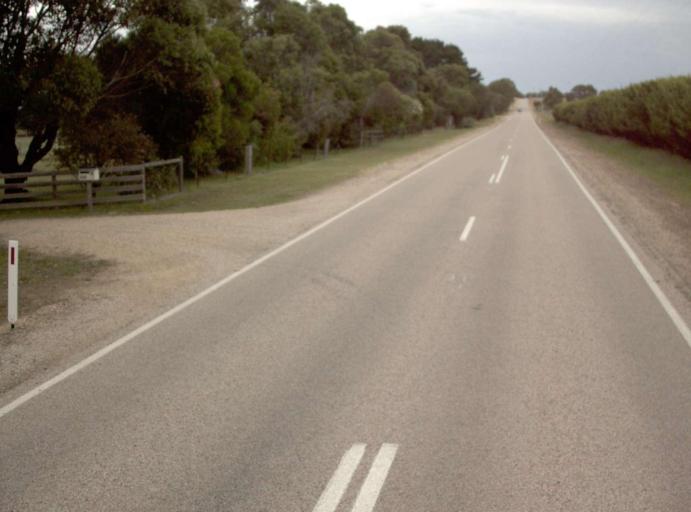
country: AU
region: Victoria
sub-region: East Gippsland
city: Bairnsdale
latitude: -37.8658
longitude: 147.5622
